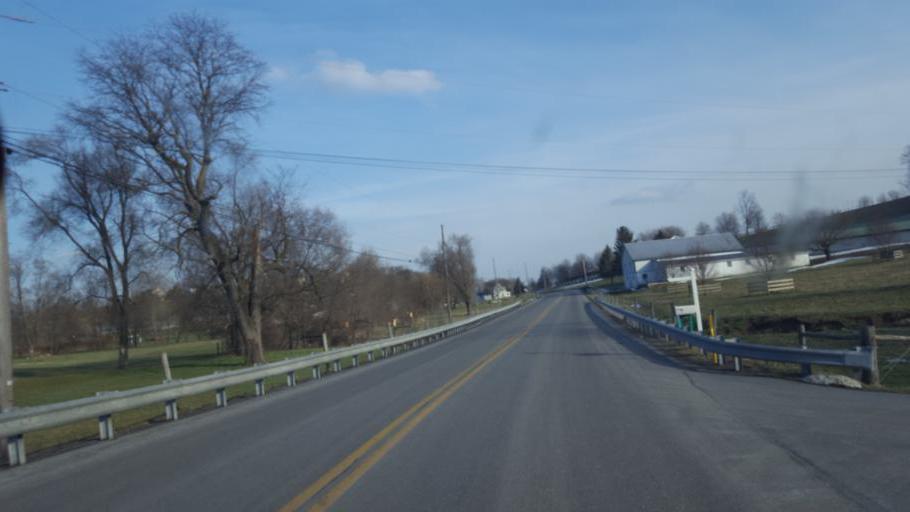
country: US
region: Pennsylvania
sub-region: Lancaster County
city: Intercourse
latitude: 40.0496
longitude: -76.1210
